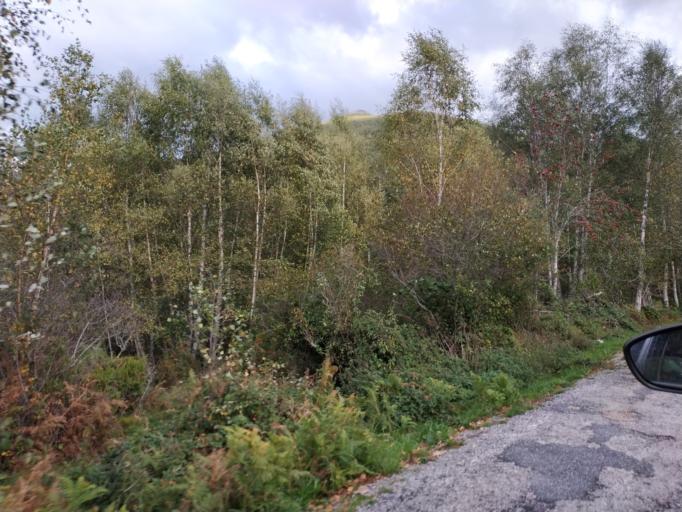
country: ES
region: Castille and Leon
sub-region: Provincia de Leon
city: Candin
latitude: 42.8632
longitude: -6.8571
